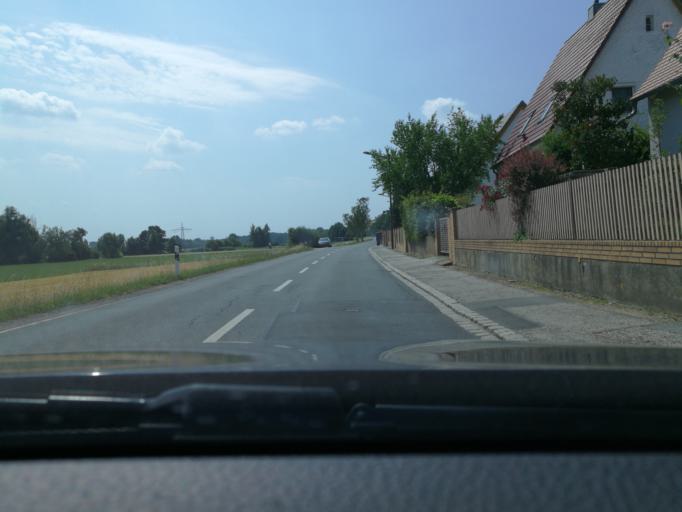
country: DE
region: Bavaria
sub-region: Regierungsbezirk Mittelfranken
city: Furth
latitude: 49.5195
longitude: 10.9643
